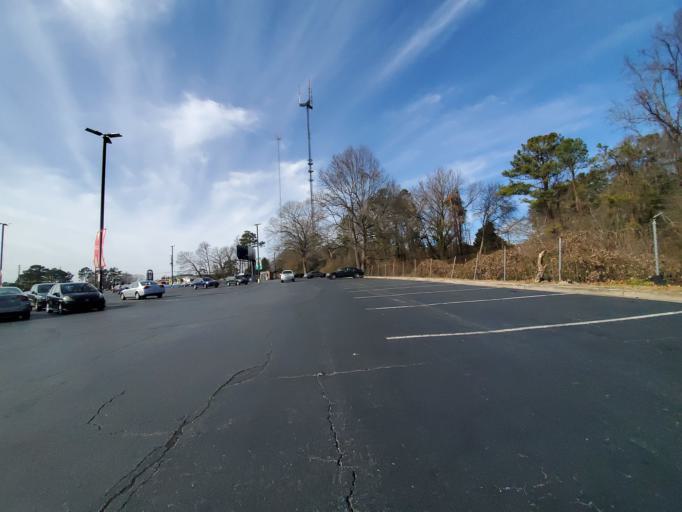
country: US
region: Georgia
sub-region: DeKalb County
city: Druid Hills
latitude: 33.8047
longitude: -84.3355
